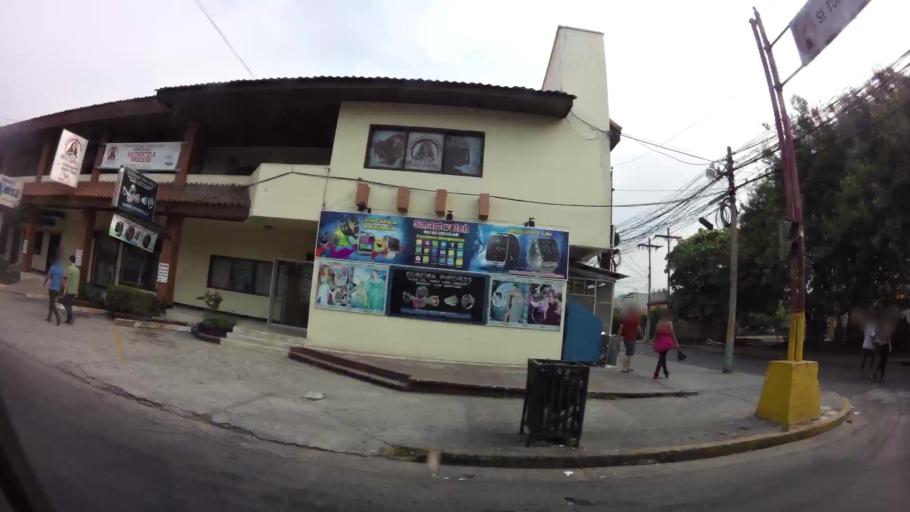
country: HN
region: Cortes
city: San Pedro Sula
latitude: 15.5061
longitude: -88.0283
